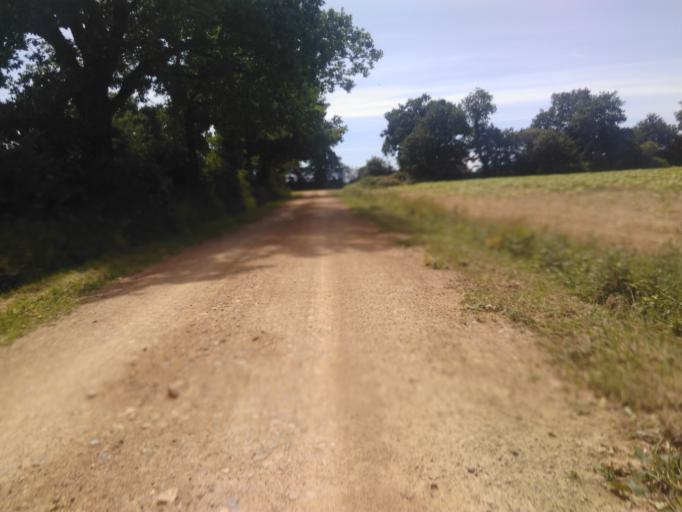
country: FR
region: Pays de la Loire
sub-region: Departement de la Vendee
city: La Ferriere
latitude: 46.7094
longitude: -1.2937
